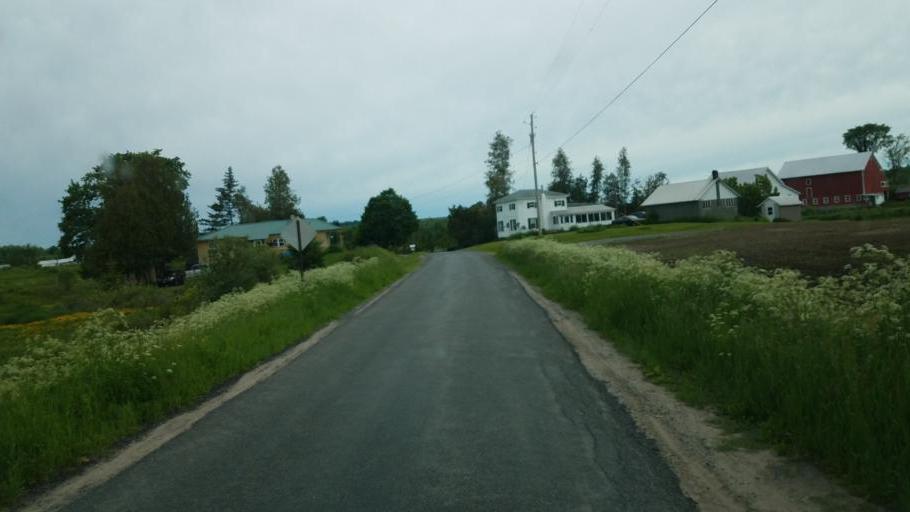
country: US
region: New York
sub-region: Herkimer County
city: Ilion
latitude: 42.9037
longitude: -75.1207
